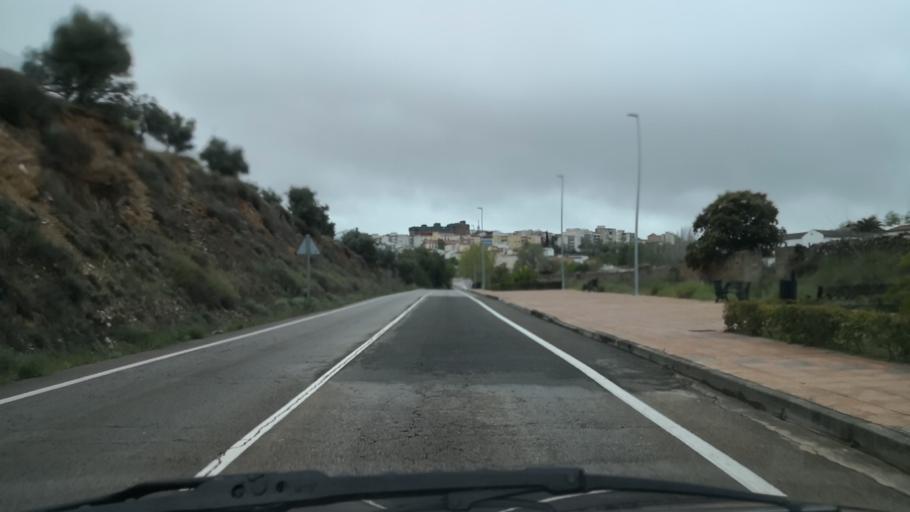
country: ES
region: Extremadura
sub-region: Provincia de Caceres
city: Caceres
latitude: 39.4838
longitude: -6.3811
